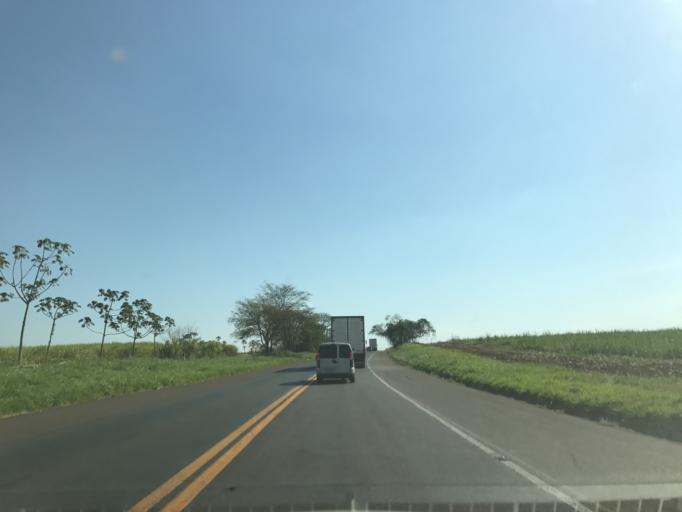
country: BR
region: Sao Paulo
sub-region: Penapolis
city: Penapolis
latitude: -21.4836
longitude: -50.2076
